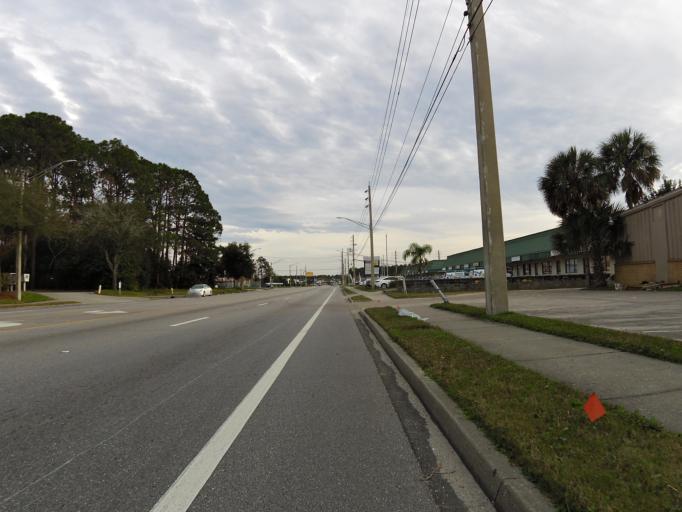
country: US
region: Florida
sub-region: Duval County
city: Jacksonville
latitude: 30.2620
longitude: -81.6210
